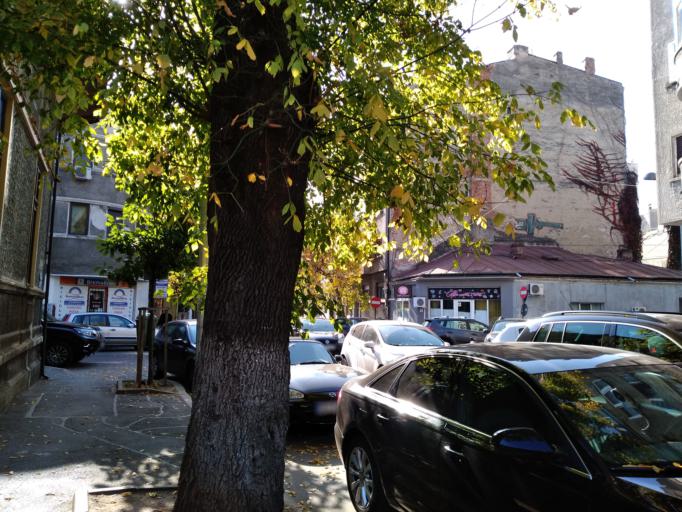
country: RO
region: Bucuresti
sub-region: Municipiul Bucuresti
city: Bucuresti
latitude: 44.4422
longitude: 26.0853
